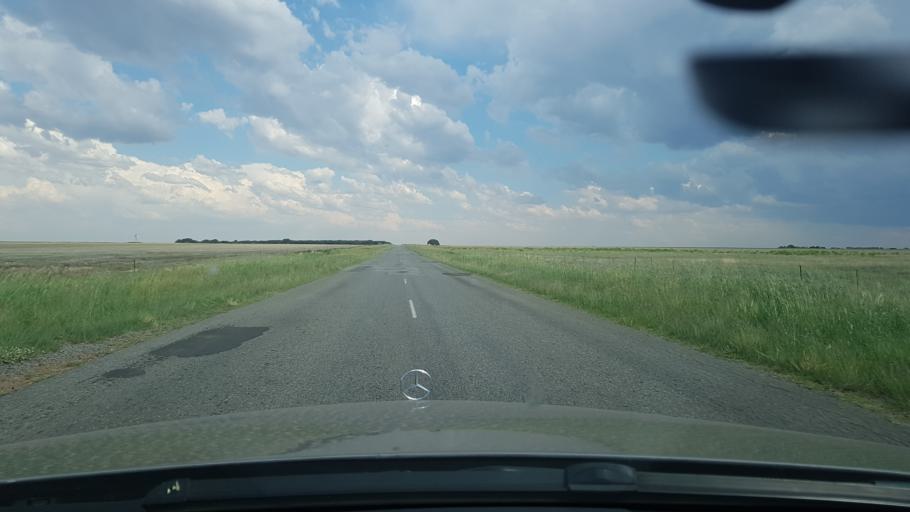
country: ZA
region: North-West
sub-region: Dr Ruth Segomotsi Mompati District Municipality
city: Bloemhof
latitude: -27.8601
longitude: 25.6525
